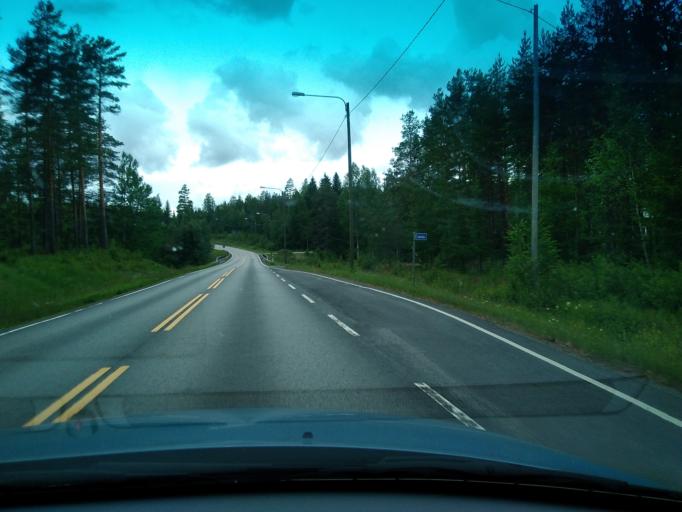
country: FI
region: Central Finland
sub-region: Saarijaervi-Viitasaari
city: Pylkoenmaeki
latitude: 62.6411
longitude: 24.8439
